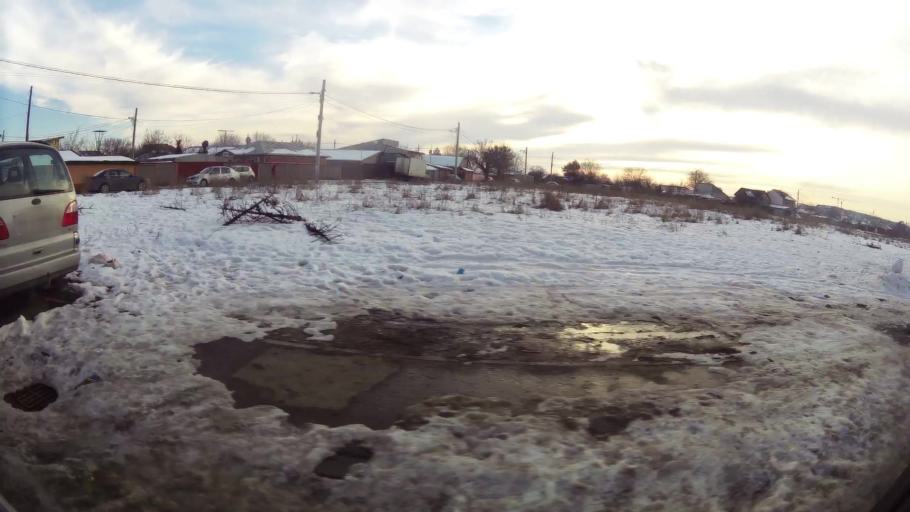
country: RO
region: Bucuresti
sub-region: Municipiul Bucuresti
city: Bucuresti
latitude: 44.3882
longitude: 26.0735
